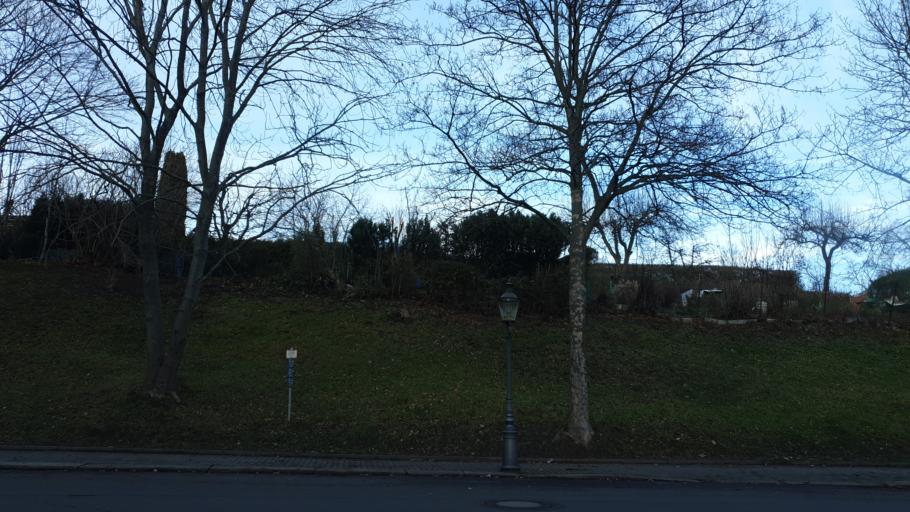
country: DE
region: Saxony
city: Chemnitz
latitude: 50.8332
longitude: 12.9479
